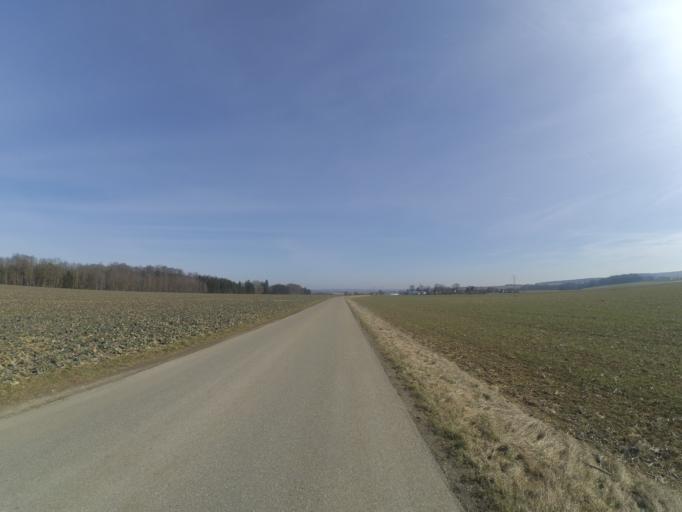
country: DE
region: Baden-Wuerttemberg
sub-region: Tuebingen Region
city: Beimerstetten
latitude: 48.4719
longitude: 10.0078
